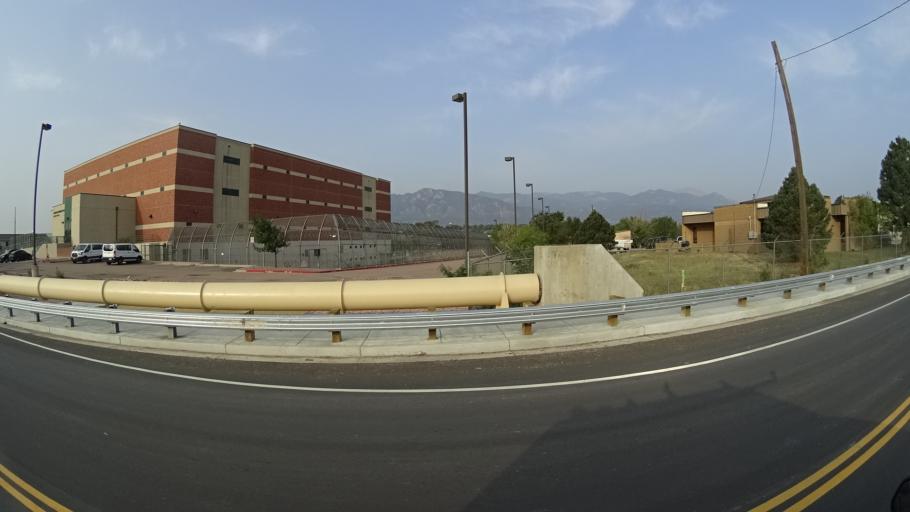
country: US
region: Colorado
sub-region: El Paso County
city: Stratmoor
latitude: 38.7836
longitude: -104.7746
